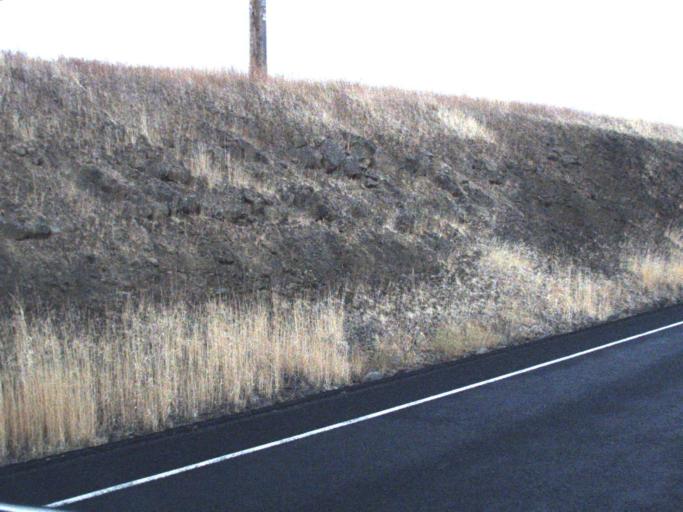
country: US
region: Washington
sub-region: Lincoln County
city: Davenport
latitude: 47.8110
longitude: -118.1793
